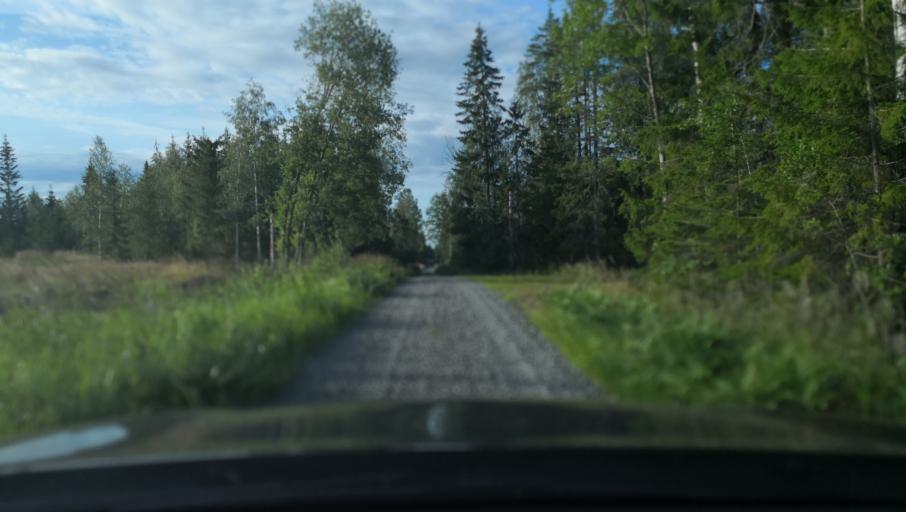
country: SE
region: Uppsala
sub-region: Osthammars Kommun
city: Osterbybruk
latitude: 60.0364
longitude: 17.9194
